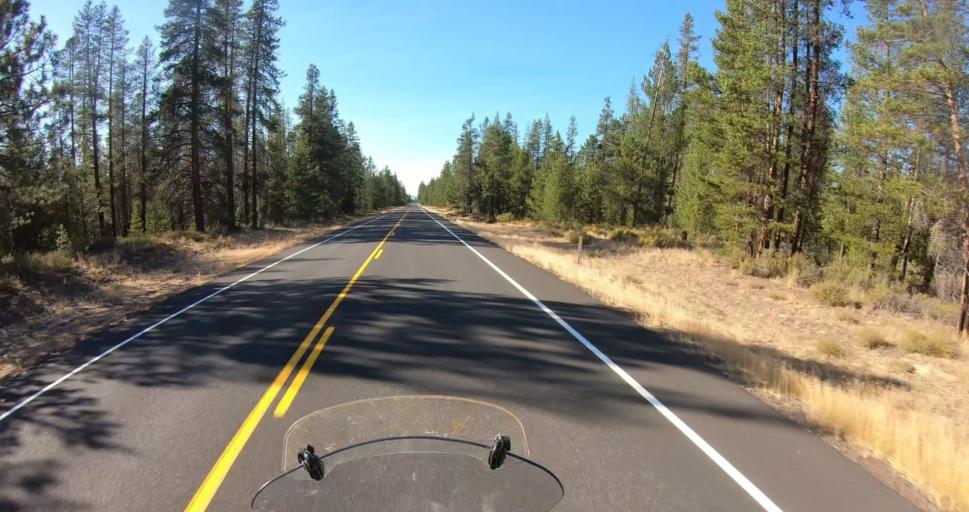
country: US
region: Oregon
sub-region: Deschutes County
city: La Pine
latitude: 43.4835
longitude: -121.4236
